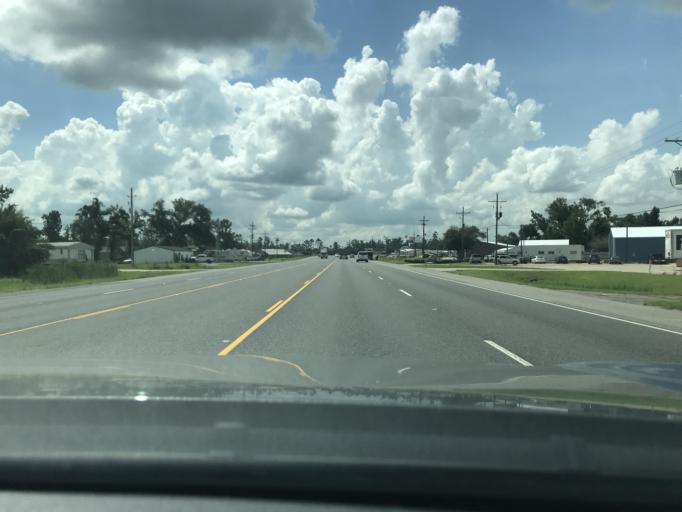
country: US
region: Louisiana
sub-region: Calcasieu Parish
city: Moss Bluff
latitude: 30.3140
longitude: -93.1972
